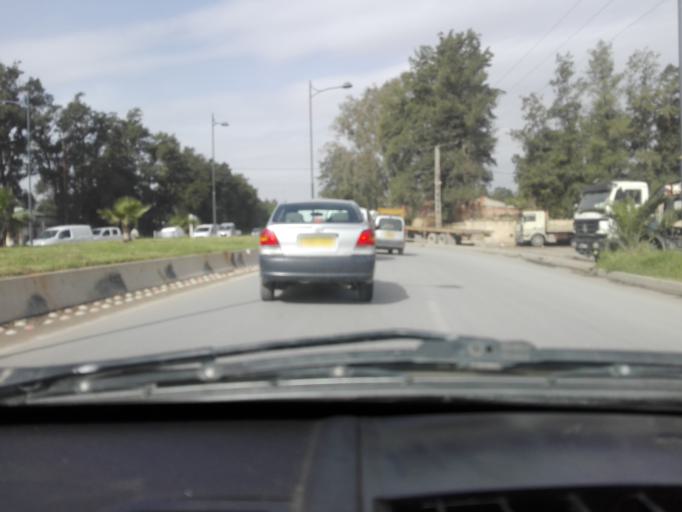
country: DZ
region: Alger
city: Dar el Beida
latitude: 36.7281
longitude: 3.2165
